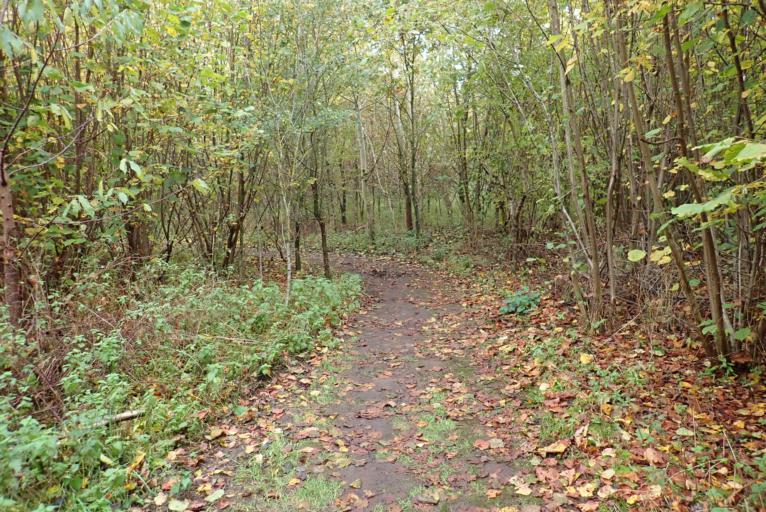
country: BE
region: Flanders
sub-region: Provincie Antwerpen
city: Sint-Katelijne-Waver
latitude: 51.0723
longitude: 4.5582
